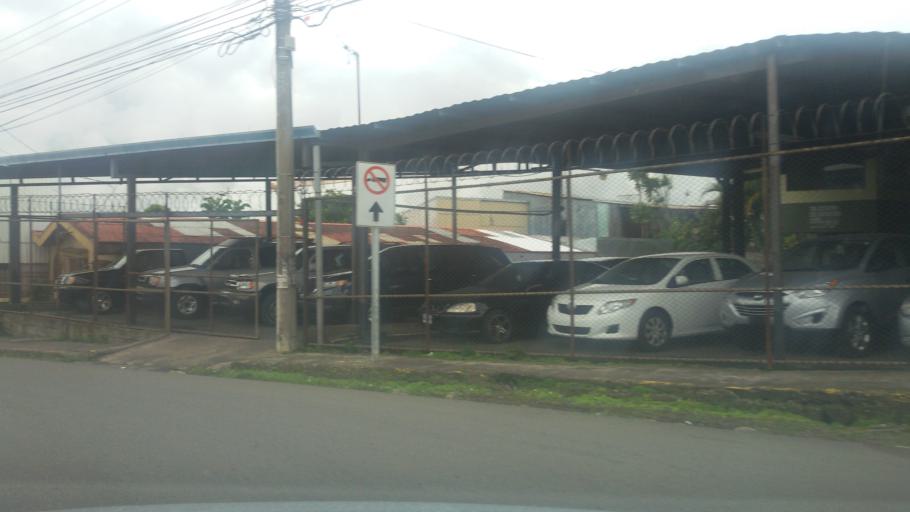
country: CR
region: Heredia
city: Angeles
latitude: 9.9822
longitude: -84.0543
